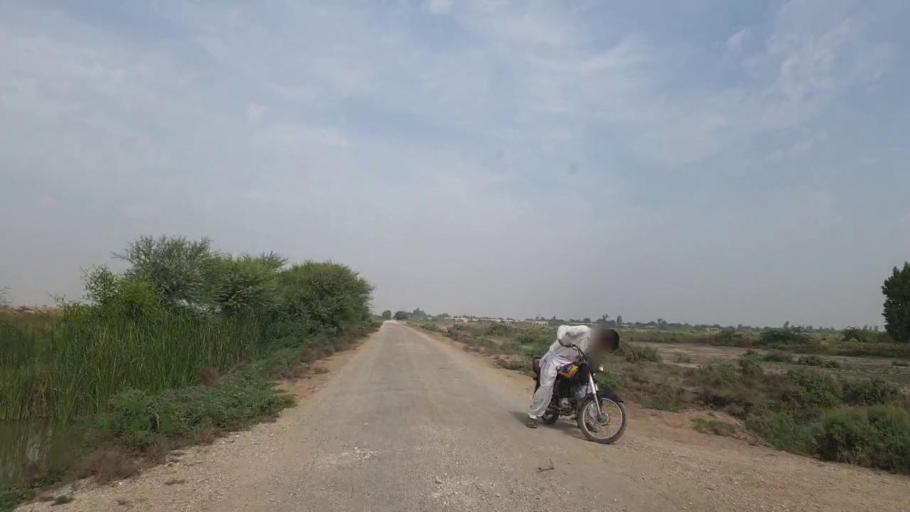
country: PK
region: Sindh
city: Rajo Khanani
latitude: 24.9826
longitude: 68.9951
